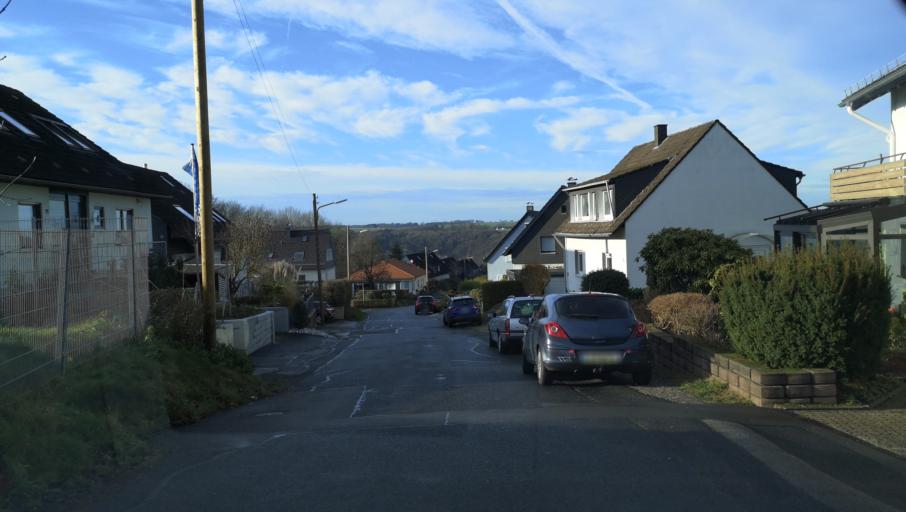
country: DE
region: North Rhine-Westphalia
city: Radevormwald
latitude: 51.2034
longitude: 7.3205
